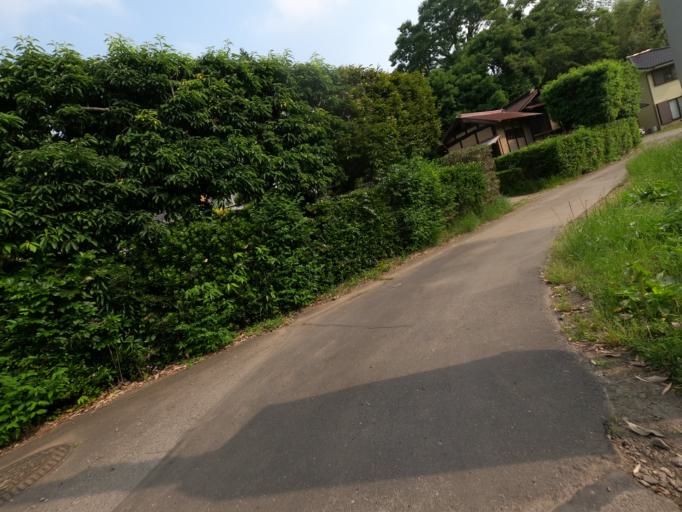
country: JP
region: Ibaraki
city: Moriya
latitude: 35.9658
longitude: 139.9538
